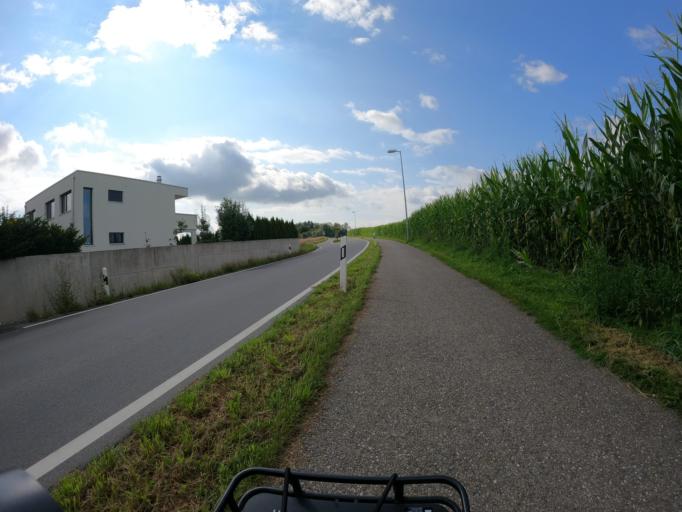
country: CH
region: Lucerne
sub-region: Hochdorf District
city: Hochdorf
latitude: 47.1588
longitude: 8.2919
